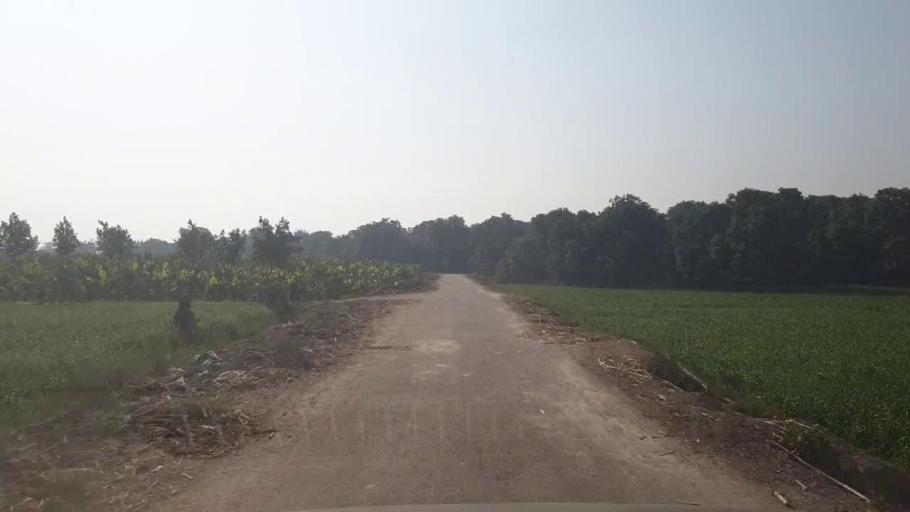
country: PK
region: Sindh
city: Tando Allahyar
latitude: 25.4679
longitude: 68.7631
